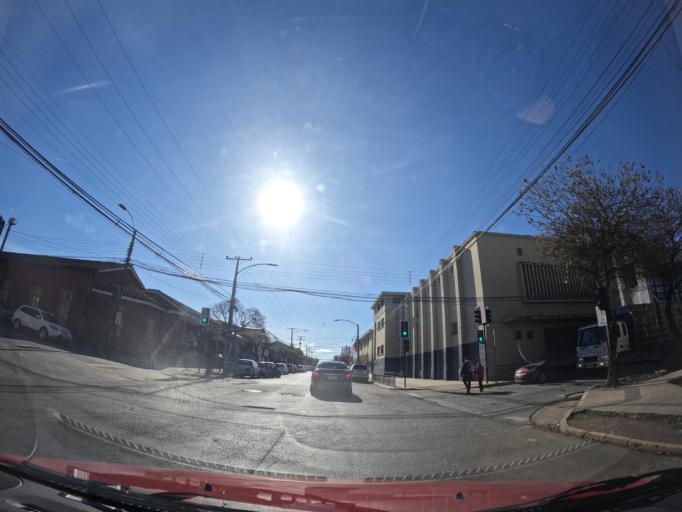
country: CL
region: Maule
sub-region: Provincia de Cauquenes
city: Cauquenes
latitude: -35.9702
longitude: -72.3148
